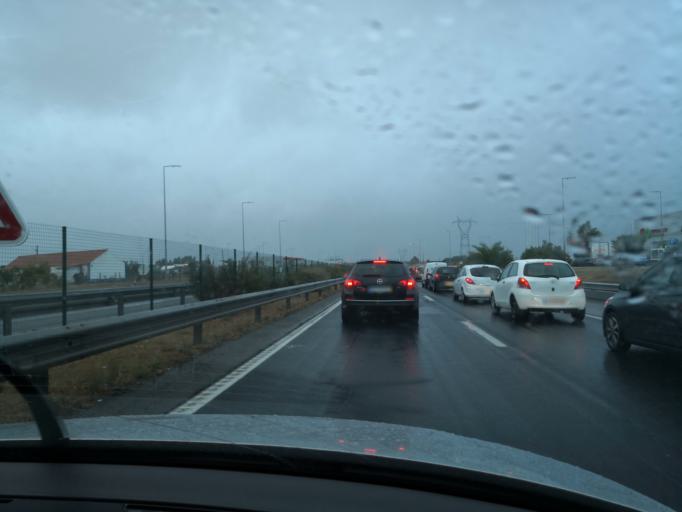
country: PT
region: Setubal
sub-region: Moita
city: Moita
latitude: 38.6632
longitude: -8.9581
